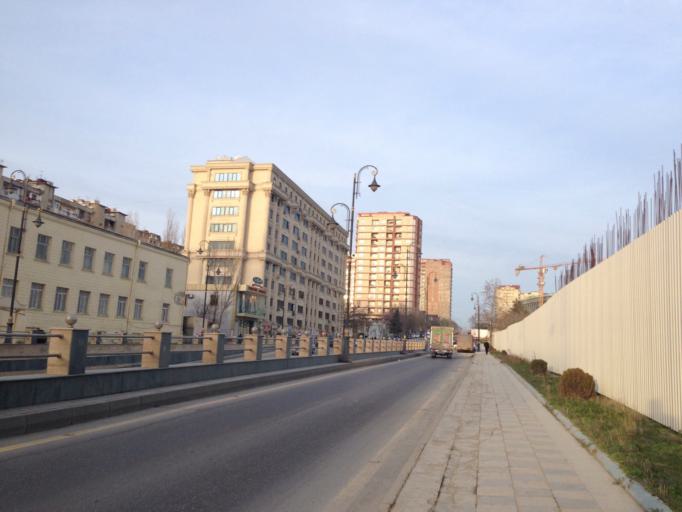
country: AZ
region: Baki
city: Baku
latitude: 40.3956
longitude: 49.8617
